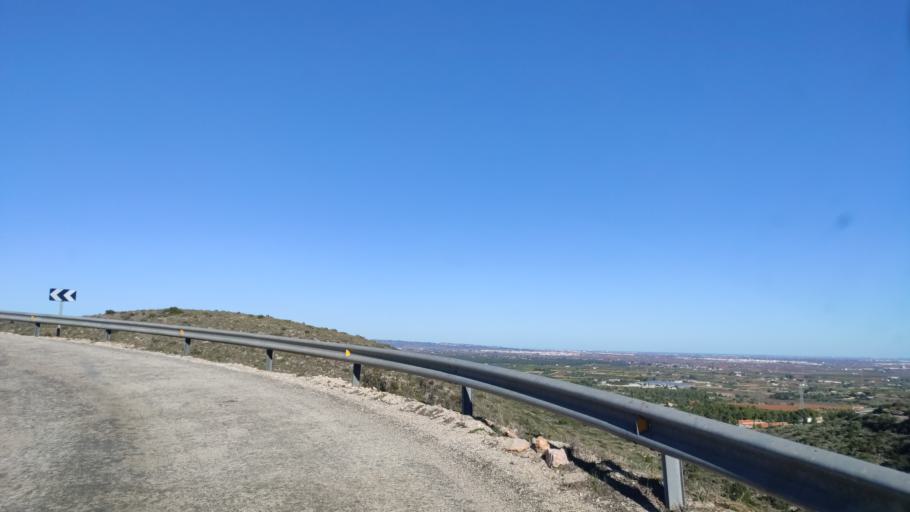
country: ES
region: Valencia
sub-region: Provincia de Valencia
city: Tous
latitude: 39.1385
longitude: -0.6024
